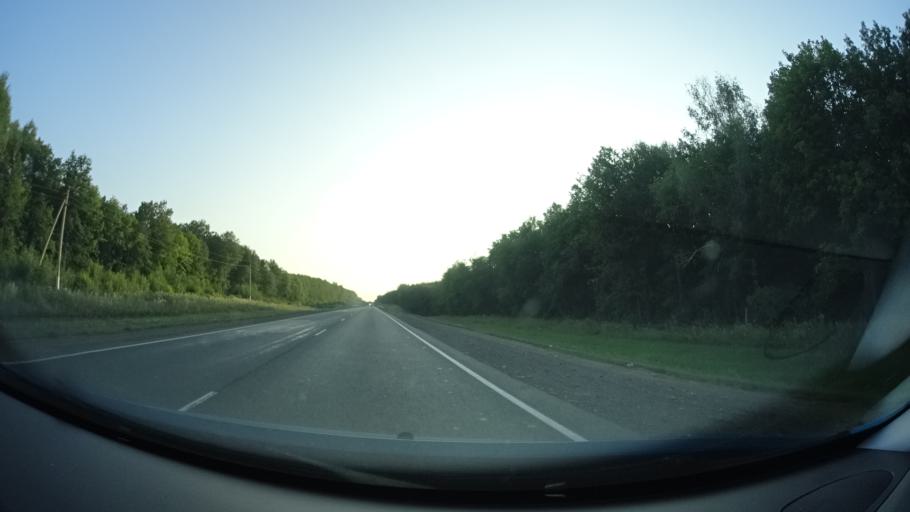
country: RU
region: Samara
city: Isakly
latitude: 54.0111
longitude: 51.6850
